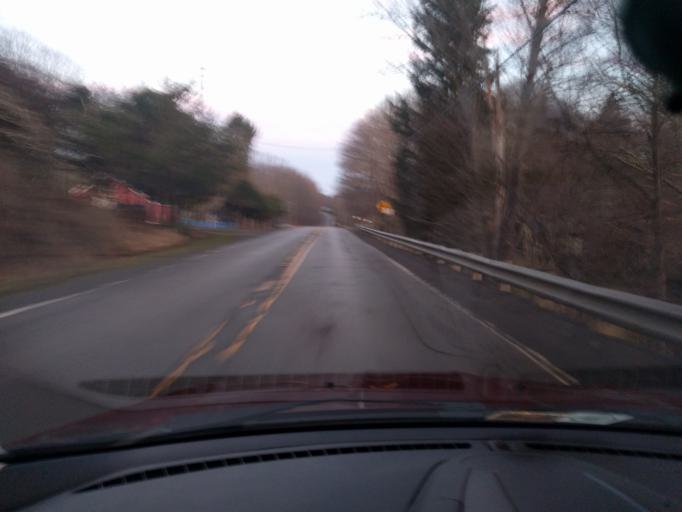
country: US
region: West Virginia
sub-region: Greenbrier County
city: Rainelle
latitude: 38.0082
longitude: -80.8792
